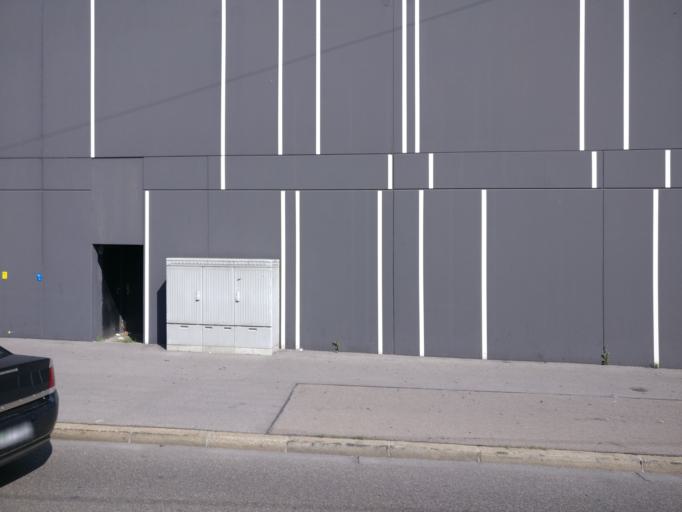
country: DE
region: Bavaria
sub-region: Swabia
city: Augsburg
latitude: 48.3848
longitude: 10.8807
